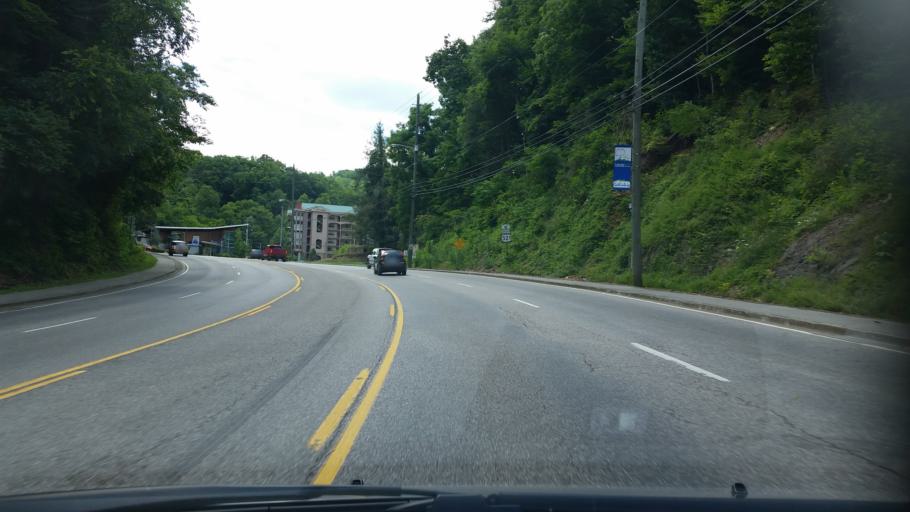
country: US
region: Tennessee
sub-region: Sevier County
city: Gatlinburg
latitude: 35.7192
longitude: -83.4995
